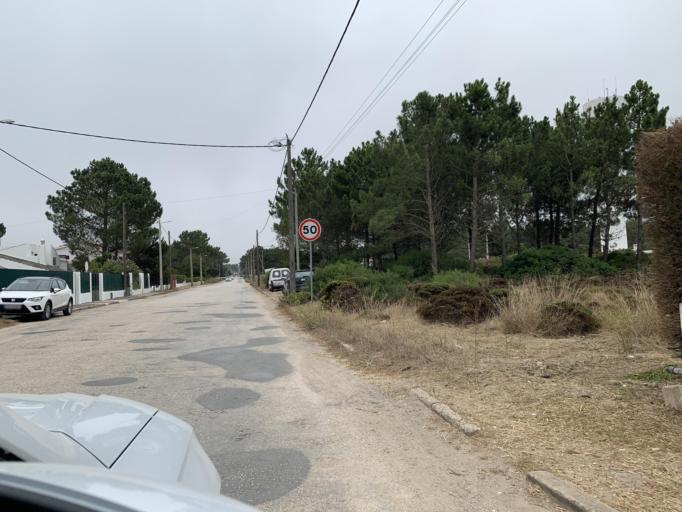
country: PT
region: Faro
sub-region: Aljezur
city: Aljezur
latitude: 37.3103
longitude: -8.8535
